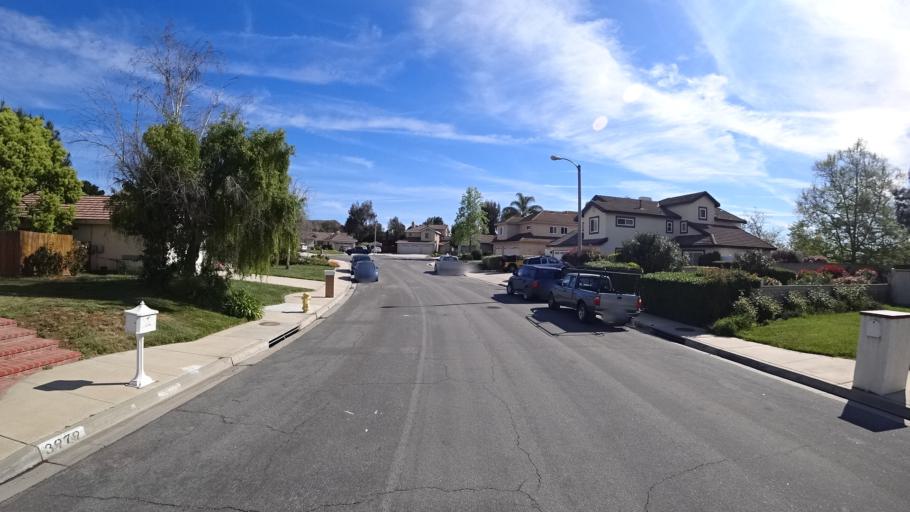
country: US
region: California
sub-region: Ventura County
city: Casa Conejo
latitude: 34.1820
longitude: -118.9585
